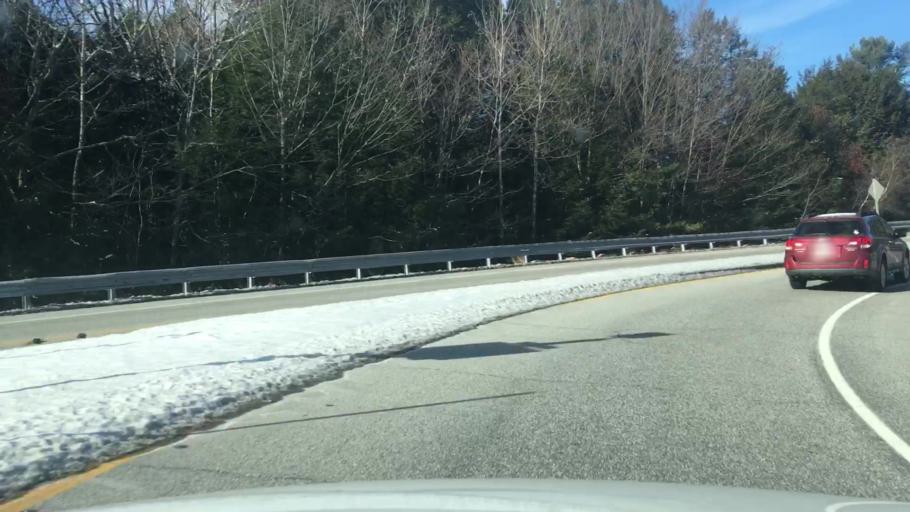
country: US
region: Maine
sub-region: Cumberland County
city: Freeport
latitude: 43.8640
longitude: -70.1094
